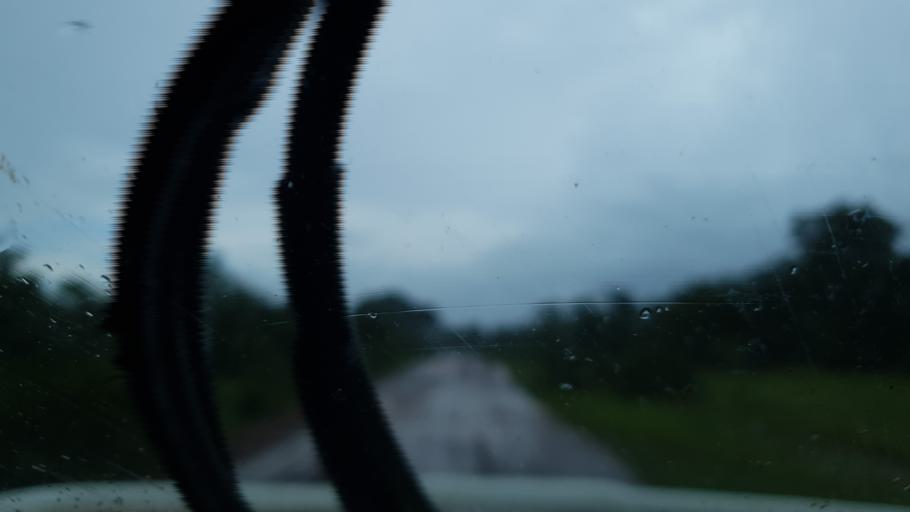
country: ML
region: Sikasso
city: Kolondieba
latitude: 11.6010
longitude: -6.6703
